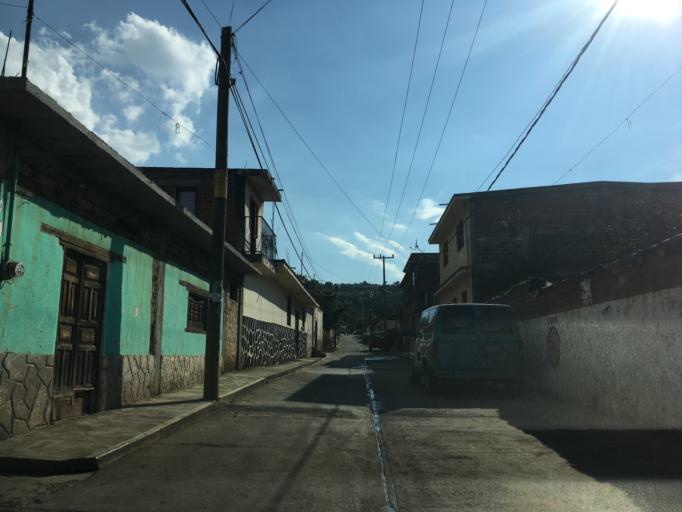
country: MX
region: Michoacan
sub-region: Patzcuaro
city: Santa Ana Chapitiro
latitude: 19.5277
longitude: -101.6536
